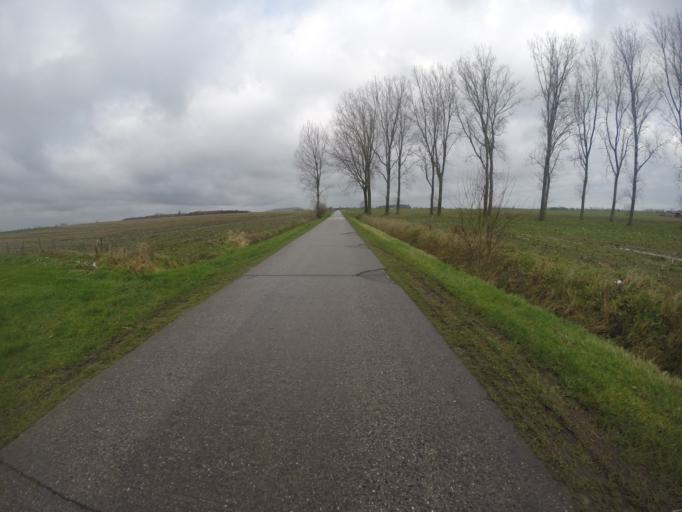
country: BE
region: Flanders
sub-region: Provincie Oost-Vlaanderen
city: Eeklo
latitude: 51.1567
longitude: 3.5056
